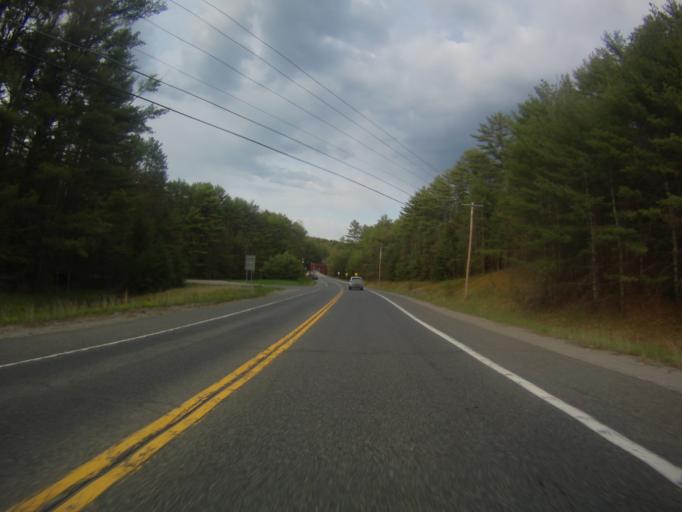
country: US
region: New York
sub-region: Warren County
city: Warrensburg
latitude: 43.6695
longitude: -73.7740
